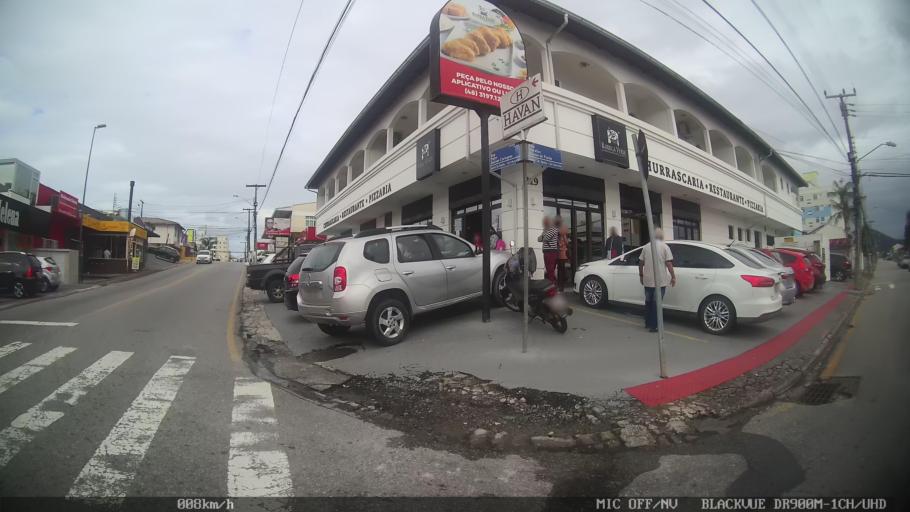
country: BR
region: Santa Catarina
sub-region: Sao Jose
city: Campinas
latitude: -27.5648
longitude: -48.6181
